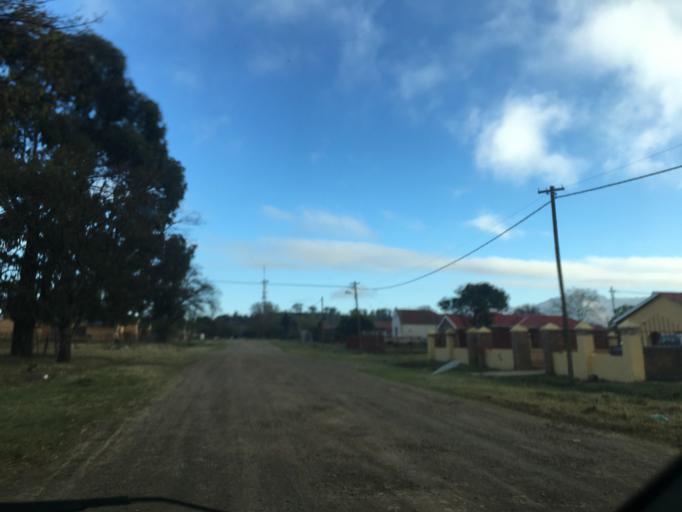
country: ZA
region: Eastern Cape
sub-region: Chris Hani District Municipality
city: Elliot
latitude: -31.3372
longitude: 27.8516
